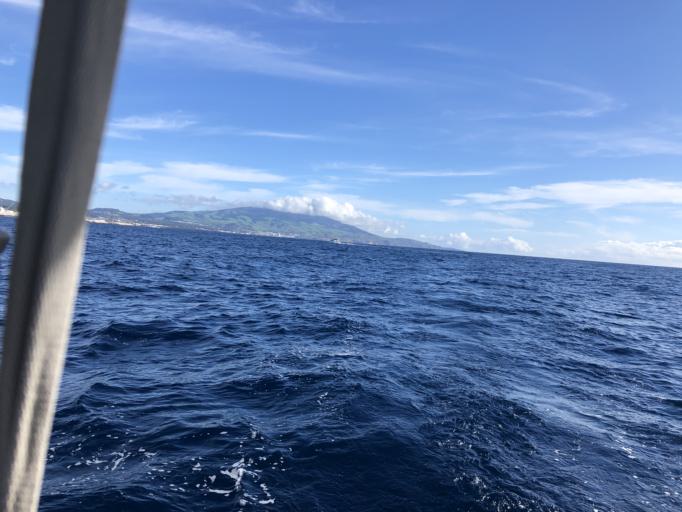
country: PT
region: Azores
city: Ponta Delgada
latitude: 37.7258
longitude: -25.6830
